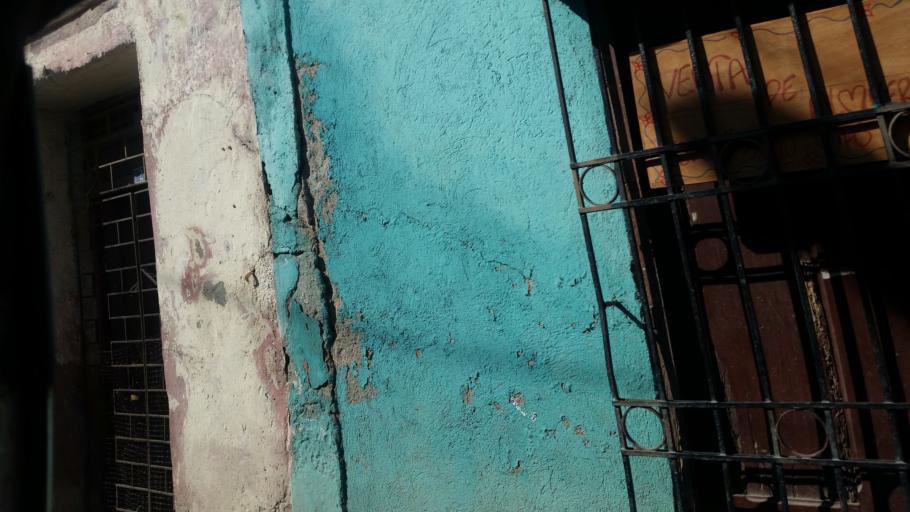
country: CO
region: Magdalena
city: Santa Marta
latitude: 11.2470
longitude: -74.2126
